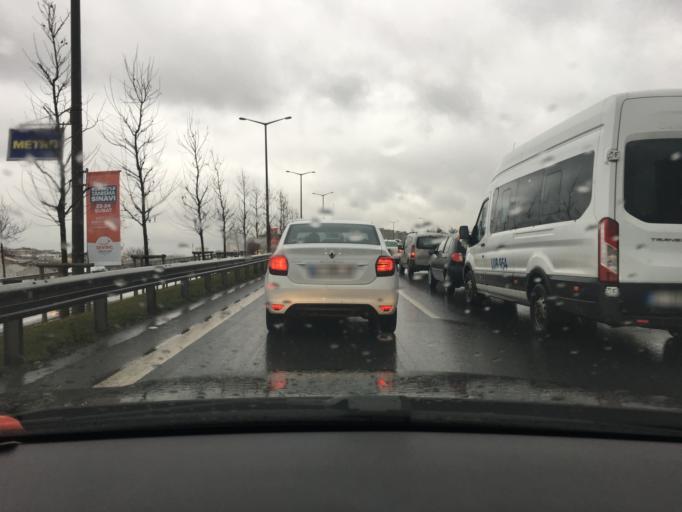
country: TR
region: Istanbul
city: Esenler
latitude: 41.0422
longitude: 28.8858
